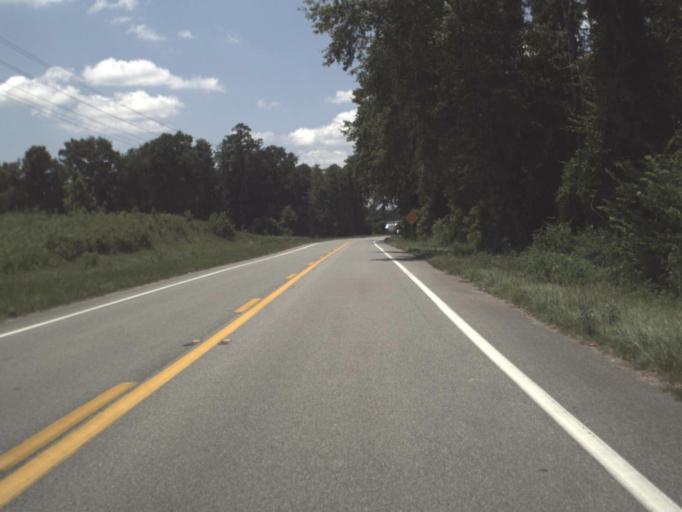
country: US
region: Florida
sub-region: Madison County
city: Madison
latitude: 30.4941
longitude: -83.6311
